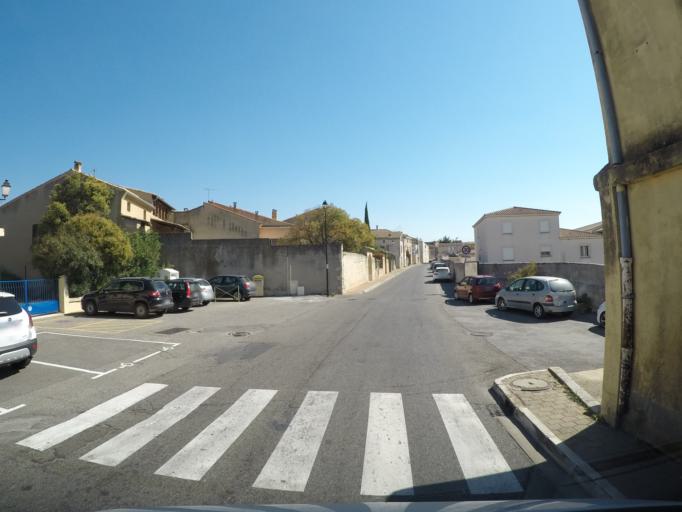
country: FR
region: Languedoc-Roussillon
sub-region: Departement du Gard
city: Tavel
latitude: 44.0123
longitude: 4.6984
